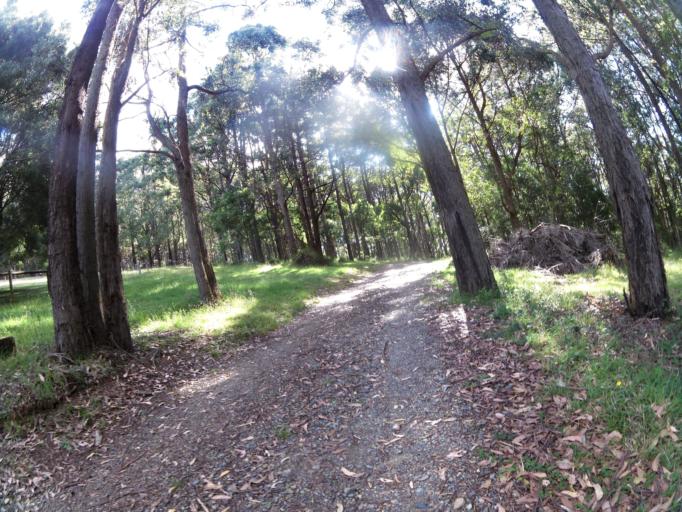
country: AU
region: Victoria
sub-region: Yarra Ranges
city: Ferny Creek
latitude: -37.8742
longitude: 145.3381
